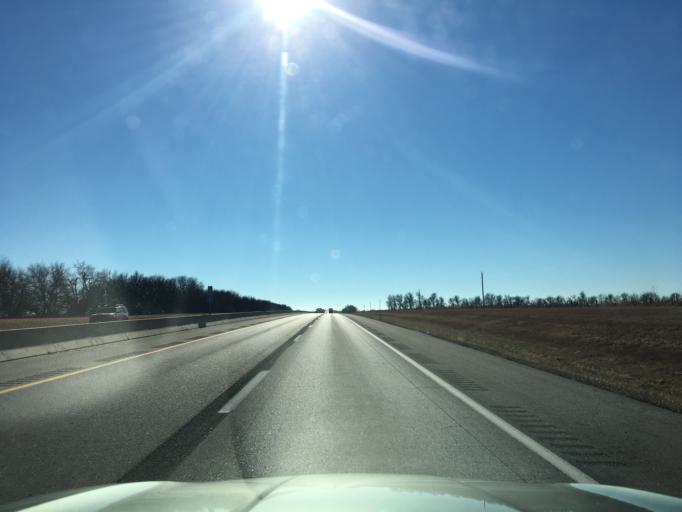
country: US
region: Kansas
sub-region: Sumner County
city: Wellington
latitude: 37.0832
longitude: -97.3386
